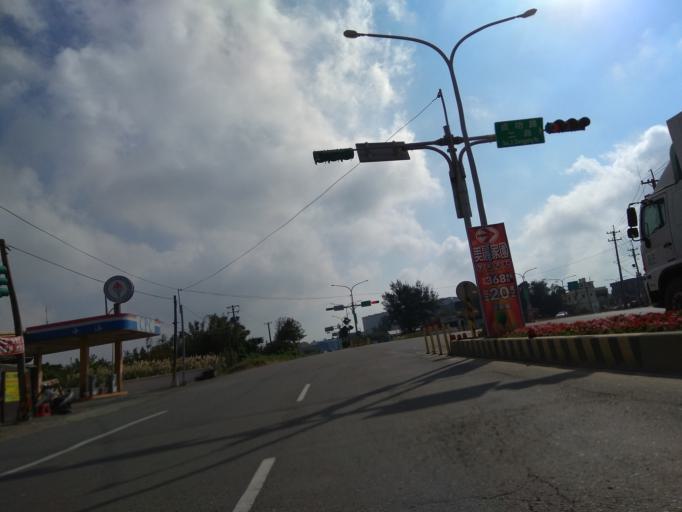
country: TW
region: Taiwan
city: Taoyuan City
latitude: 25.0365
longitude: 121.1032
